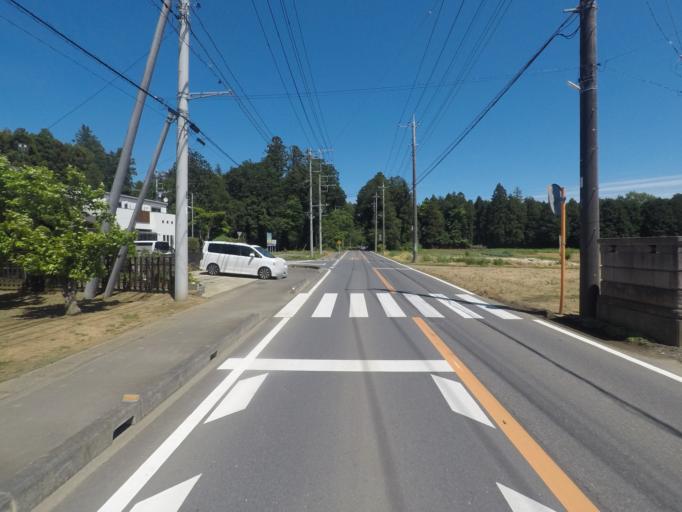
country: JP
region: Ibaraki
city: Ami
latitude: 36.0973
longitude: 140.2468
